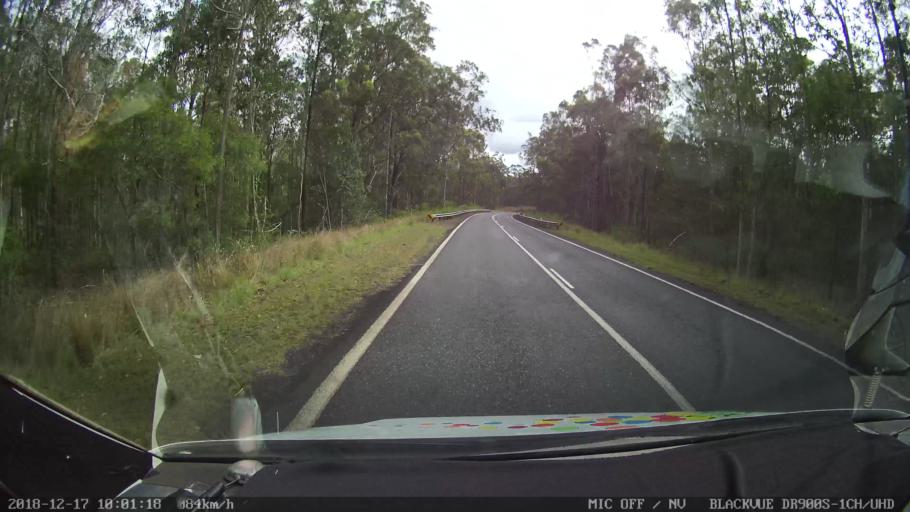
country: AU
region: New South Wales
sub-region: Tenterfield Municipality
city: Carrolls Creek
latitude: -28.9057
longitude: 152.4366
